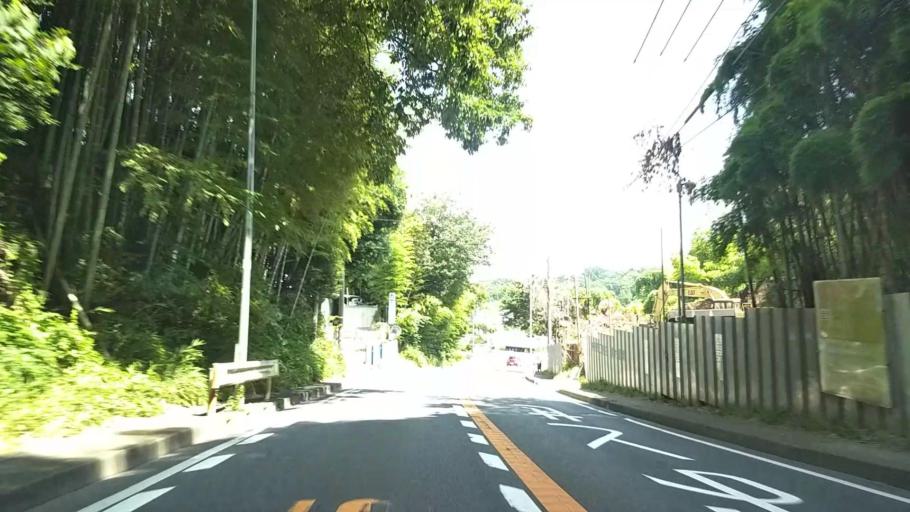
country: JP
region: Kanagawa
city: Fujisawa
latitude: 35.3714
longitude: 139.5156
